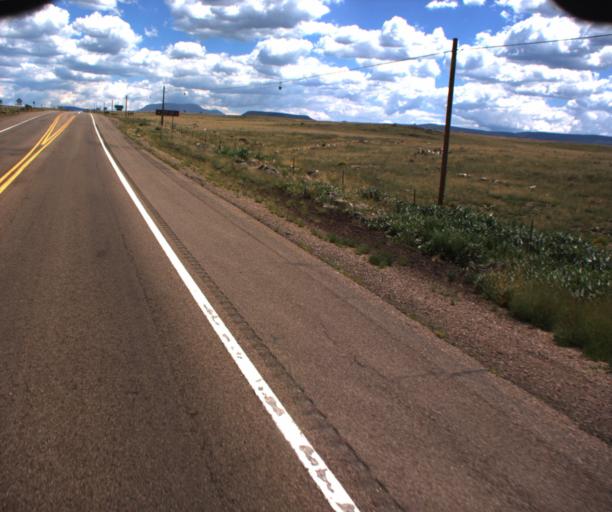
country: US
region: Arizona
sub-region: Apache County
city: Springerville
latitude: 34.1760
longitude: -109.3208
